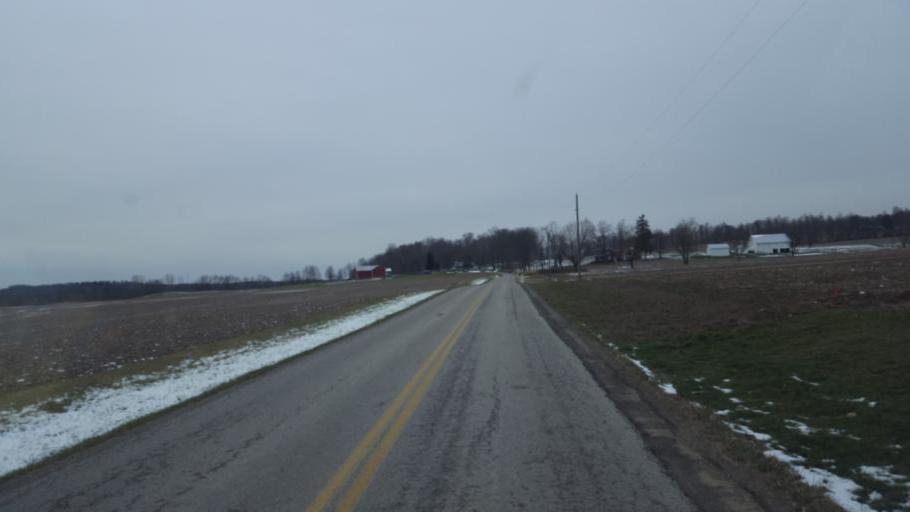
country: US
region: Ohio
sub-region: Richland County
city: Lexington
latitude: 40.7015
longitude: -82.5858
